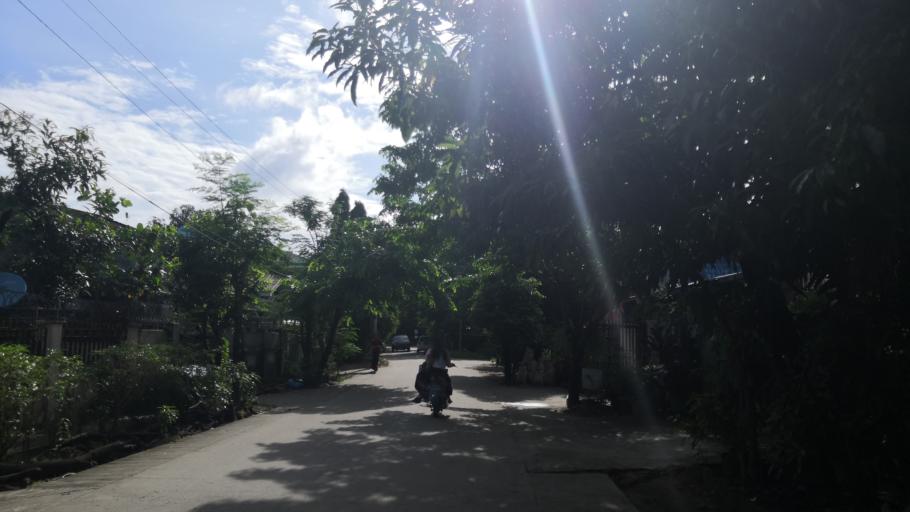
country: MM
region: Yangon
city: Yangon
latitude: 16.8664
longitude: 96.1821
